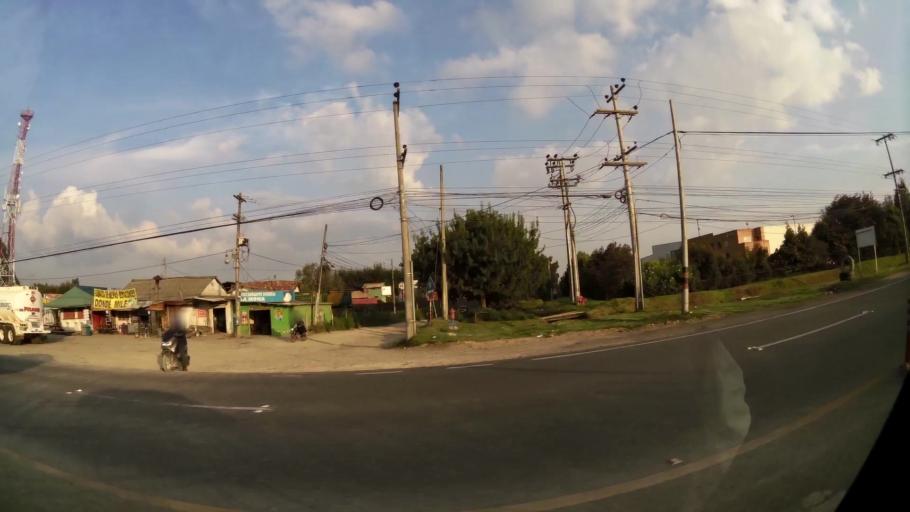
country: CO
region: Cundinamarca
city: Cota
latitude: 4.7639
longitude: -74.1525
